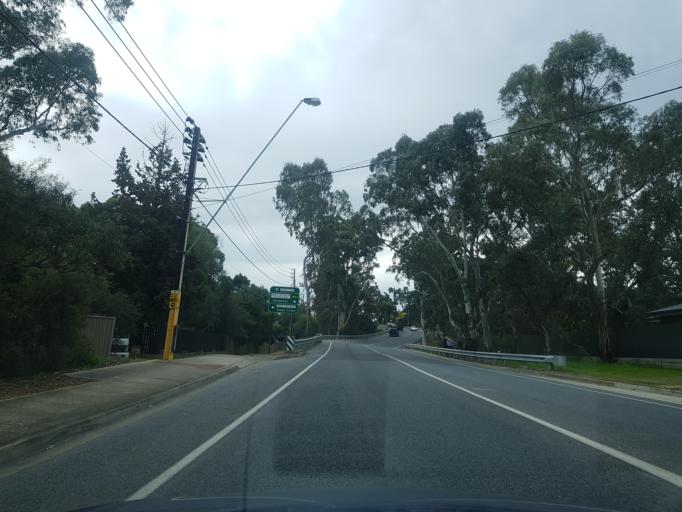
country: AU
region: South Australia
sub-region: Tea Tree Gully
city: Hope Valley
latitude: -34.8423
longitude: 138.7203
